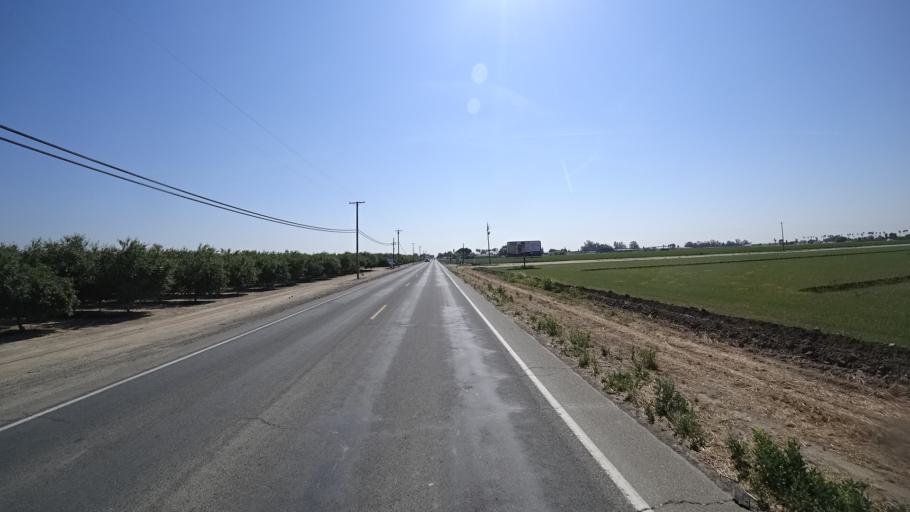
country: US
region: California
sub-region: Kings County
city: Lemoore
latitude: 36.3424
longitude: -119.8178
